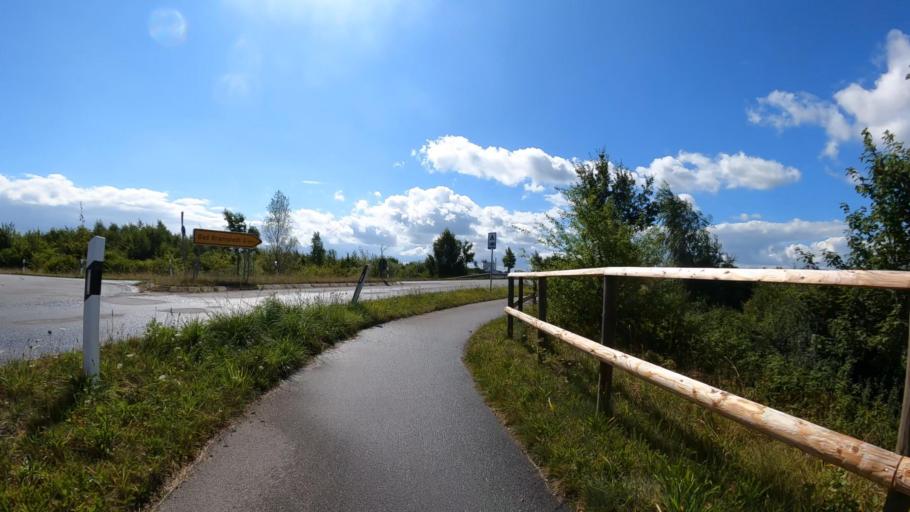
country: DE
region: Schleswig-Holstein
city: Fuhlendorf
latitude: 53.9342
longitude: 9.8918
